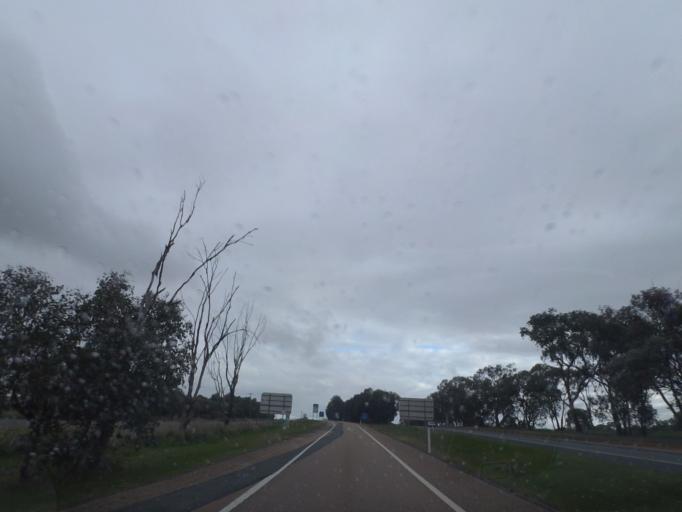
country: AU
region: Victoria
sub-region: Wangaratta
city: Wangaratta
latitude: -36.2192
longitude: 146.4475
